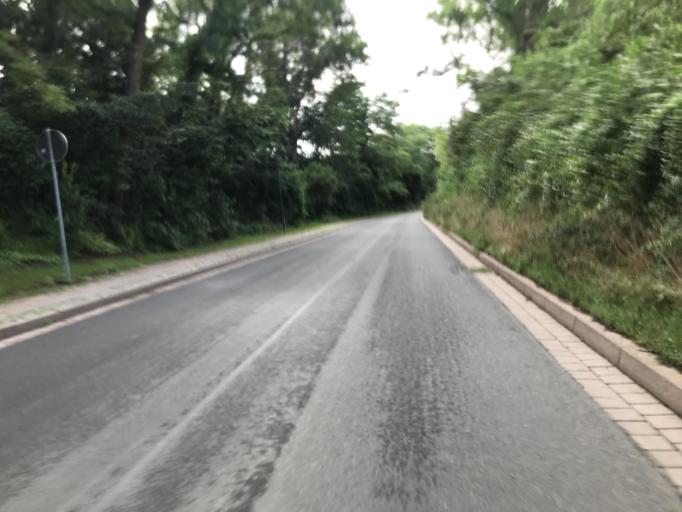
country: DE
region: Saxony-Anhalt
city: Ditfurt
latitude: 51.8320
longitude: 11.2032
